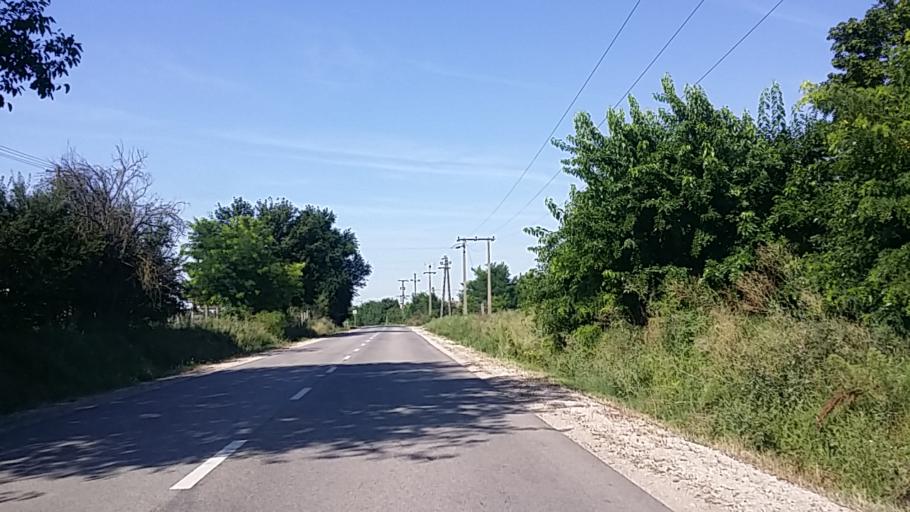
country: HU
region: Fejer
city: Pusztaszabolcs
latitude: 47.1150
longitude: 18.7746
